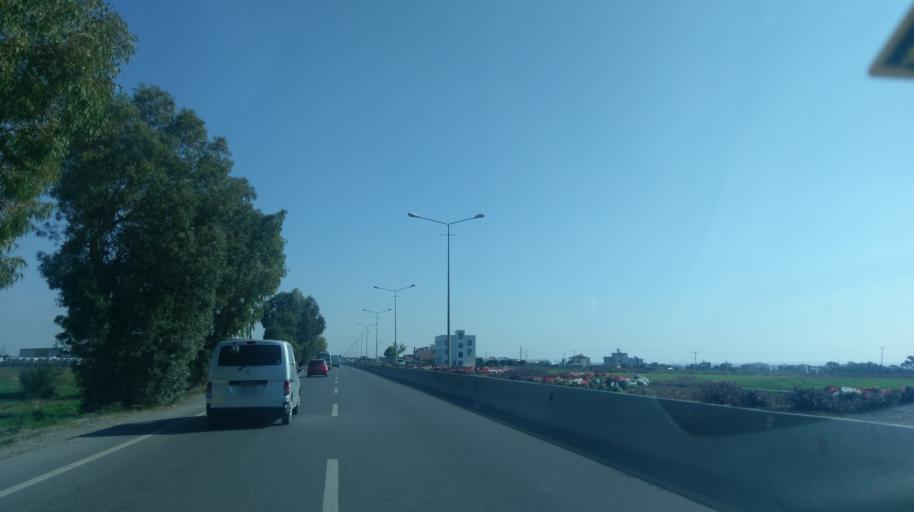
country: CY
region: Lefkosia
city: Nicosia
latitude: 35.2216
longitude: 33.4868
